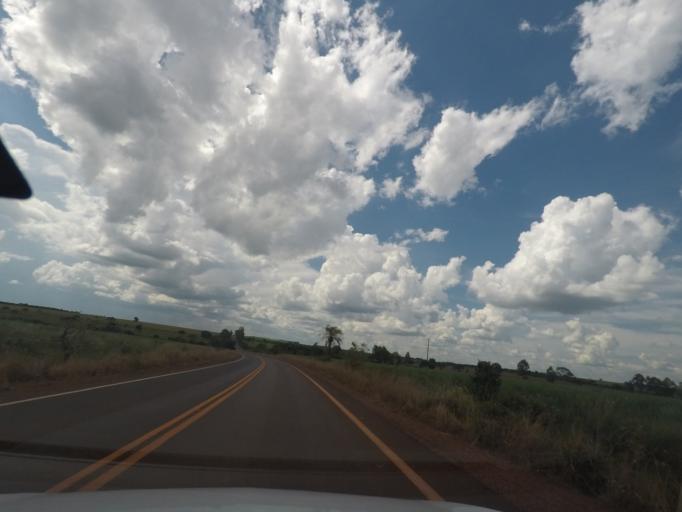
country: BR
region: Minas Gerais
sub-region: Conceicao Das Alagoas
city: Conceicao das Alagoas
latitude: -19.8024
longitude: -48.5806
